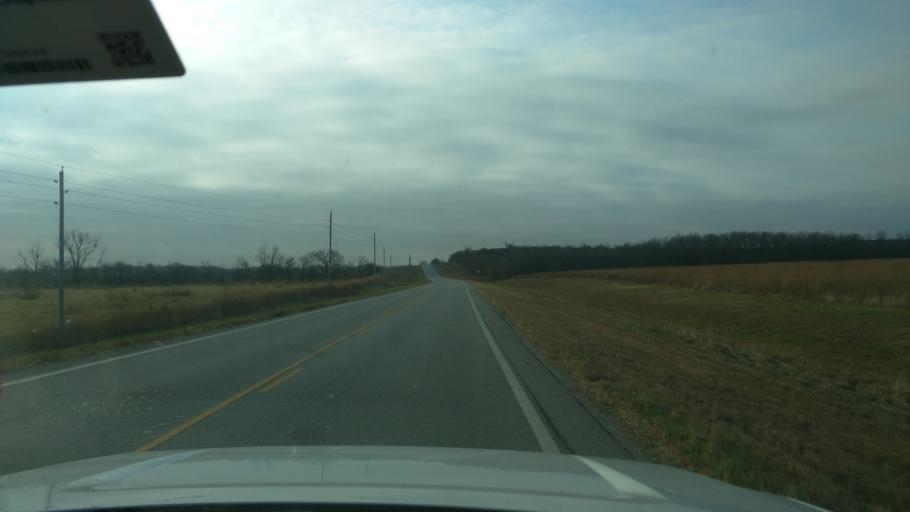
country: US
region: Kansas
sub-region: Greenwood County
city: Eureka
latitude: 37.7358
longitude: -96.2297
